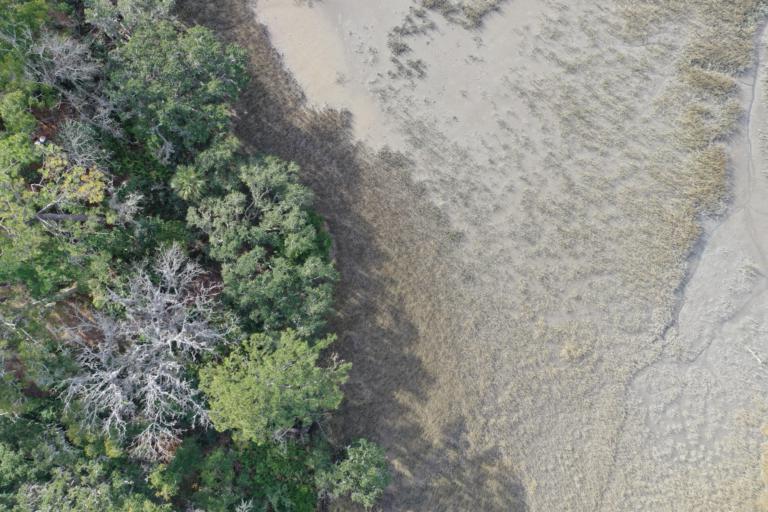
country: US
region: Georgia
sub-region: Chatham County
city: Montgomery
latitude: 31.9323
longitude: -81.0982
